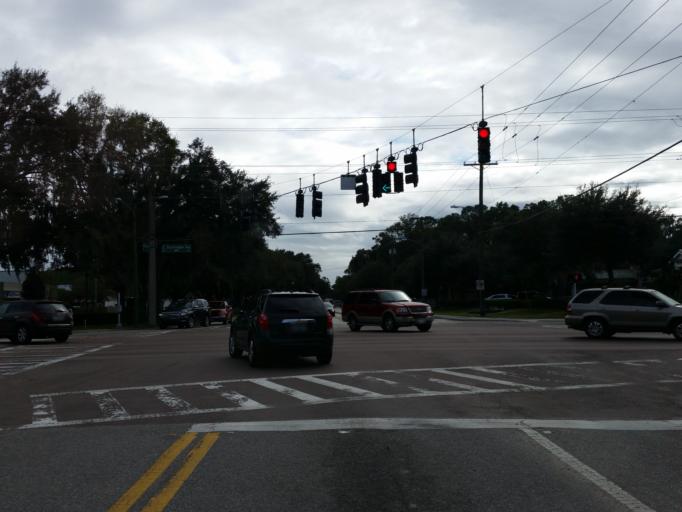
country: US
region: Florida
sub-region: Hillsborough County
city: Brandon
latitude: 27.8939
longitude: -82.2857
